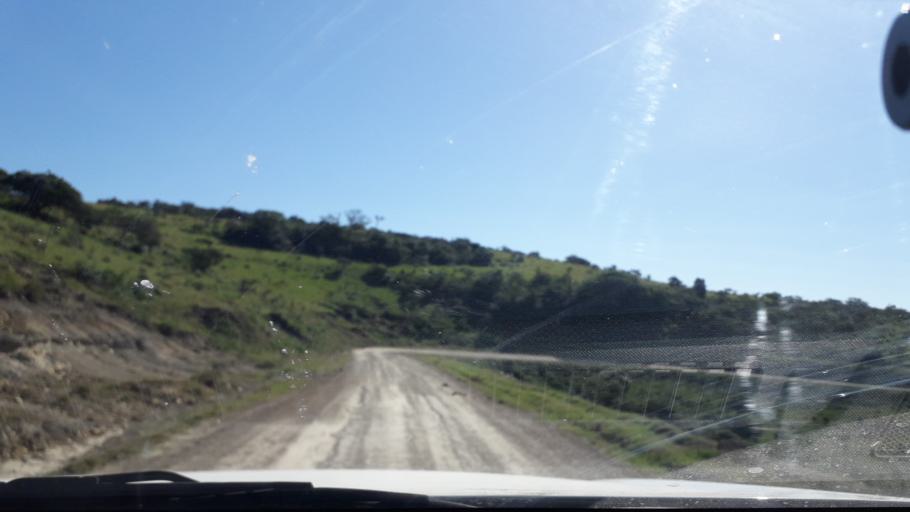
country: ZA
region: Eastern Cape
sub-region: Amathole District Municipality
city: Komga
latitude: -32.7892
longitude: 27.9527
